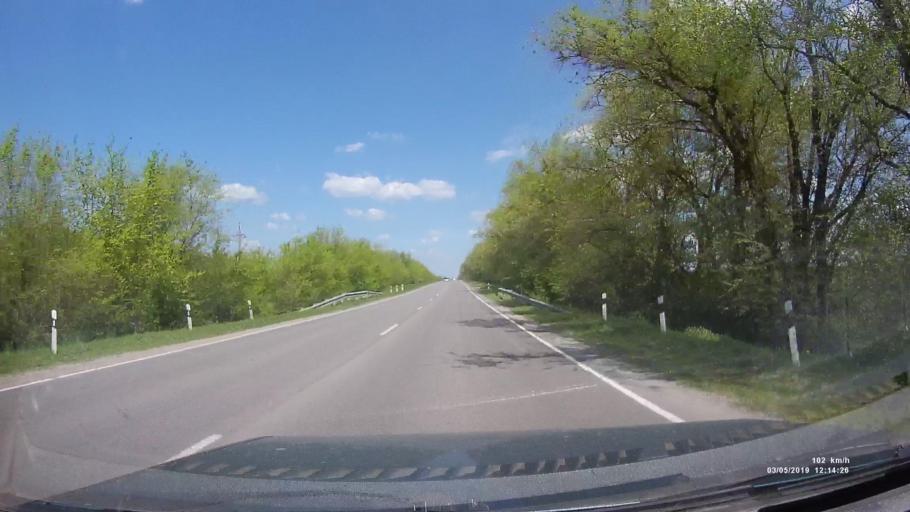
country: RU
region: Rostov
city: Melikhovskaya
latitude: 47.3440
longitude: 40.5634
